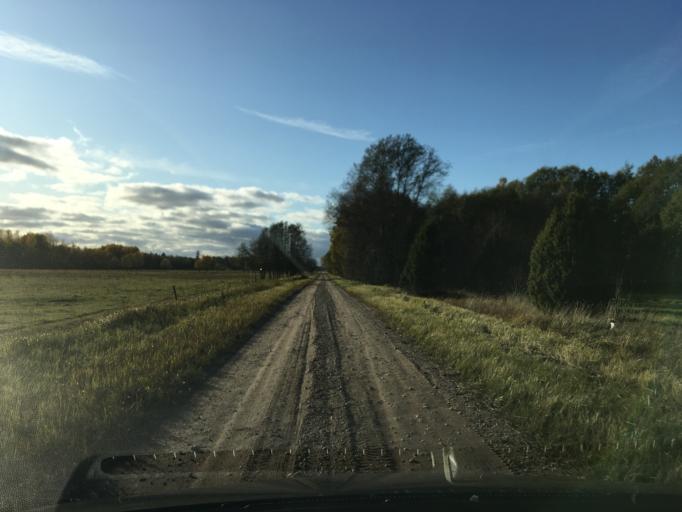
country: EE
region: Laeaene
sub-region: Lihula vald
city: Lihula
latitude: 58.5635
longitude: 23.8129
